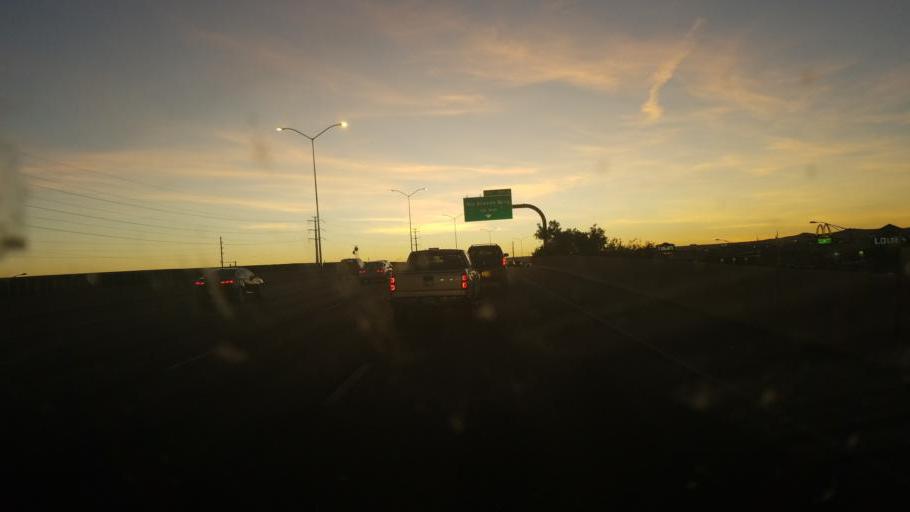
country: US
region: New Mexico
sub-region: Bernalillo County
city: Albuquerque
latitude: 35.1066
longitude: -106.6566
